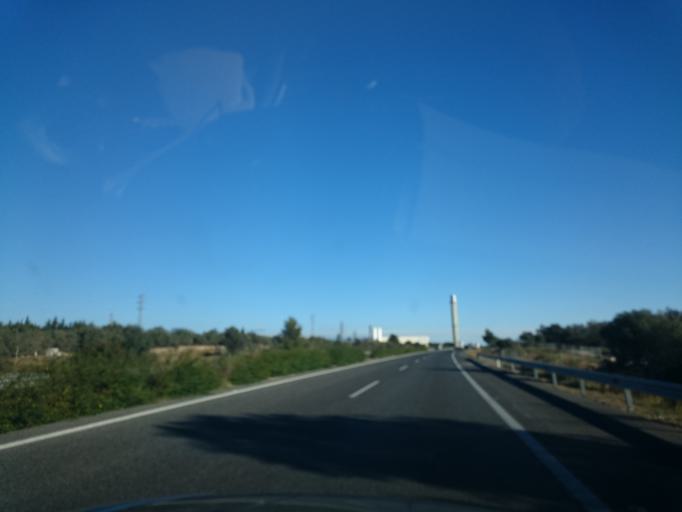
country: ES
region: Catalonia
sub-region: Provincia de Tarragona
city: Camarles
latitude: 40.7965
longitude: 0.6685
